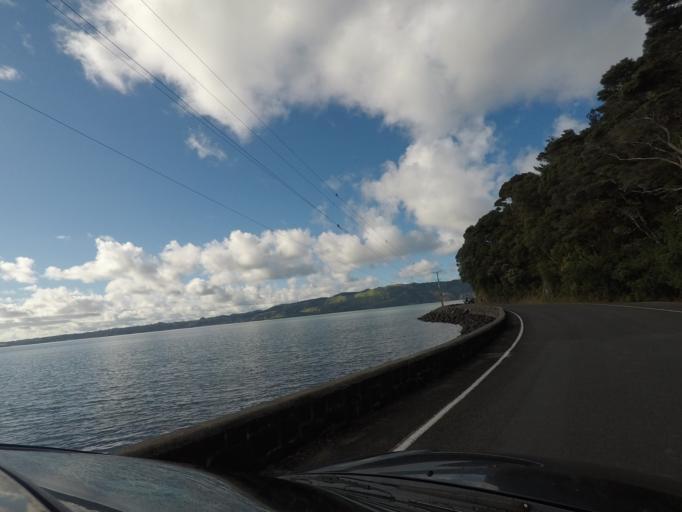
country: NZ
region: Auckland
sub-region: Auckland
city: Titirangi
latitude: -37.0097
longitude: 174.5627
